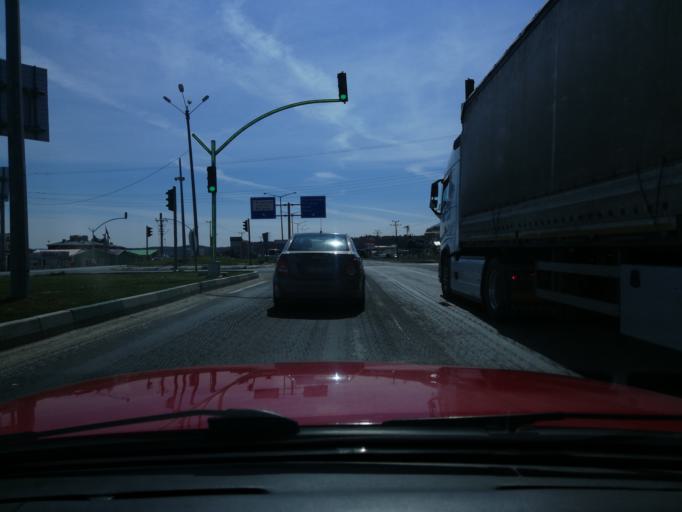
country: TR
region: Kuetahya
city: Kutahya
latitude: 39.3840
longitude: 30.0434
